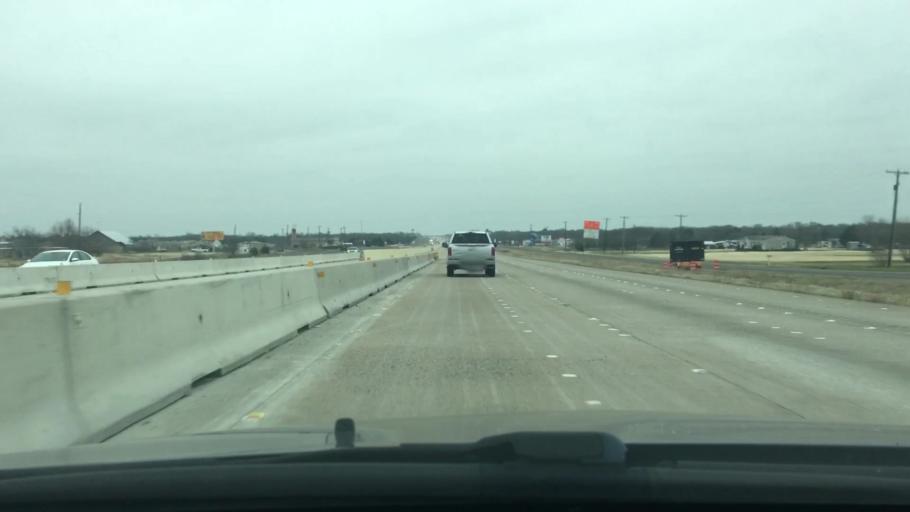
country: US
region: Texas
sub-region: Navarro County
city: Corsicana
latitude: 32.0293
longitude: -96.4424
